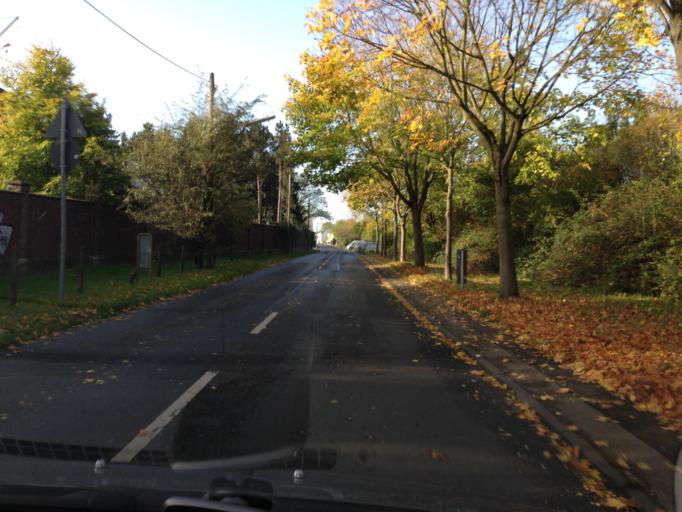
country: DE
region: North Rhine-Westphalia
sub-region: Regierungsbezirk Koln
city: Gremberghoven
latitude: 50.8993
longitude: 7.0425
